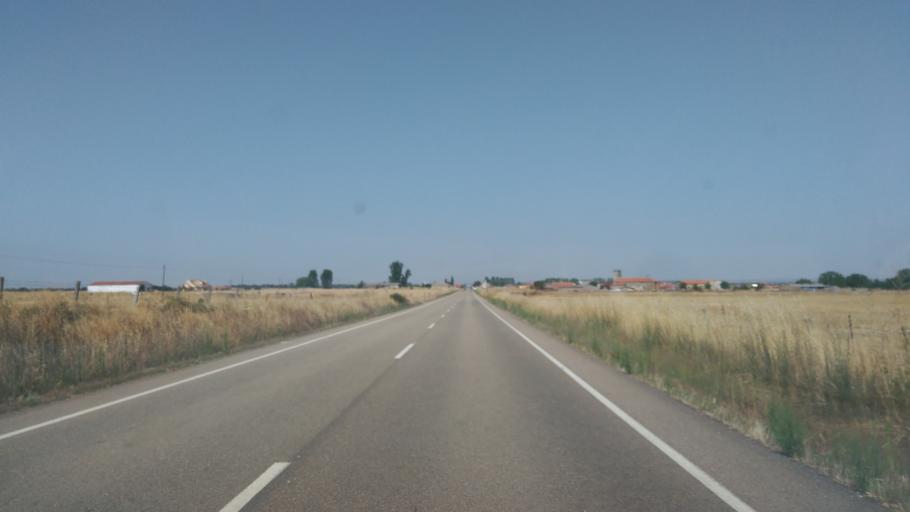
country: ES
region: Castille and Leon
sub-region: Provincia de Salamanca
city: La Fuente de San Esteban
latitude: 40.7724
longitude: -6.2251
